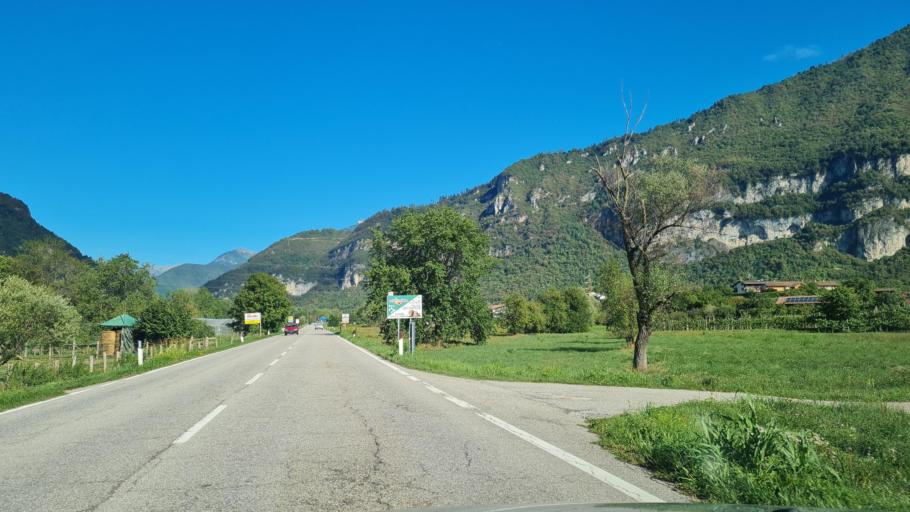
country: IT
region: Veneto
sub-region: Provincia di Belluno
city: Fonzaso
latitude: 46.0079
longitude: 11.7992
